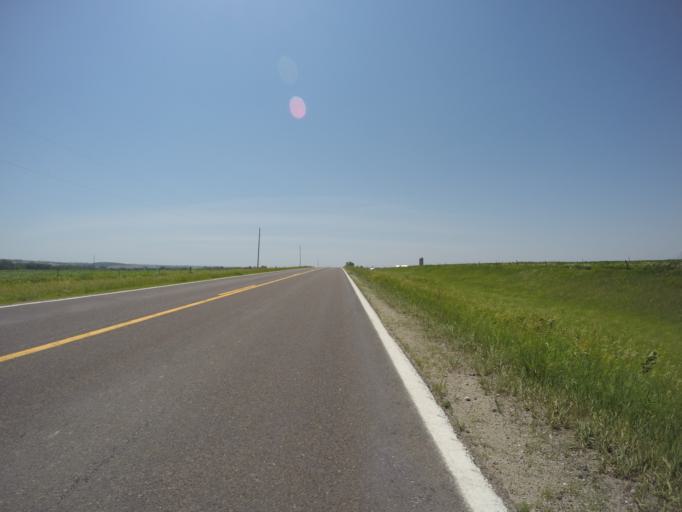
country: US
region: Nebraska
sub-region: Pawnee County
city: Pawnee City
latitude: 40.0201
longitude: -96.0484
